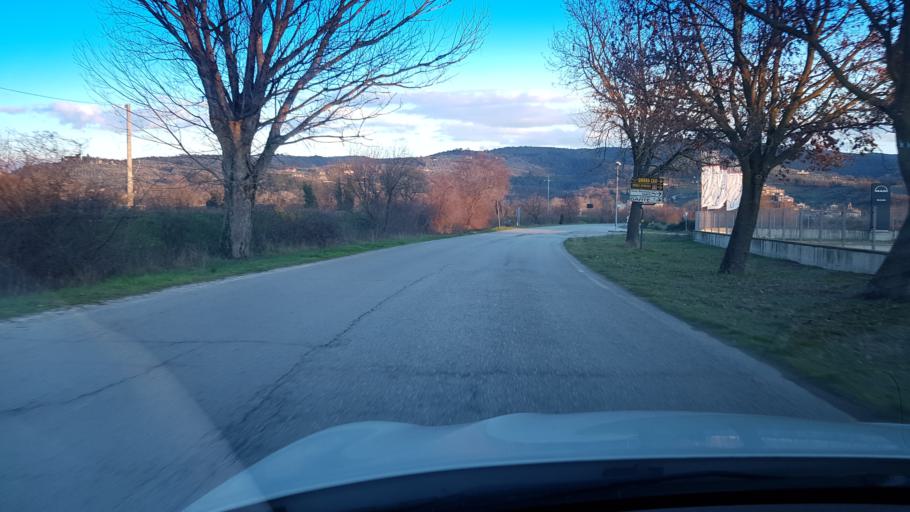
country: IT
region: Umbria
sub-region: Provincia di Perugia
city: Torgiano
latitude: 43.0186
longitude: 12.4226
